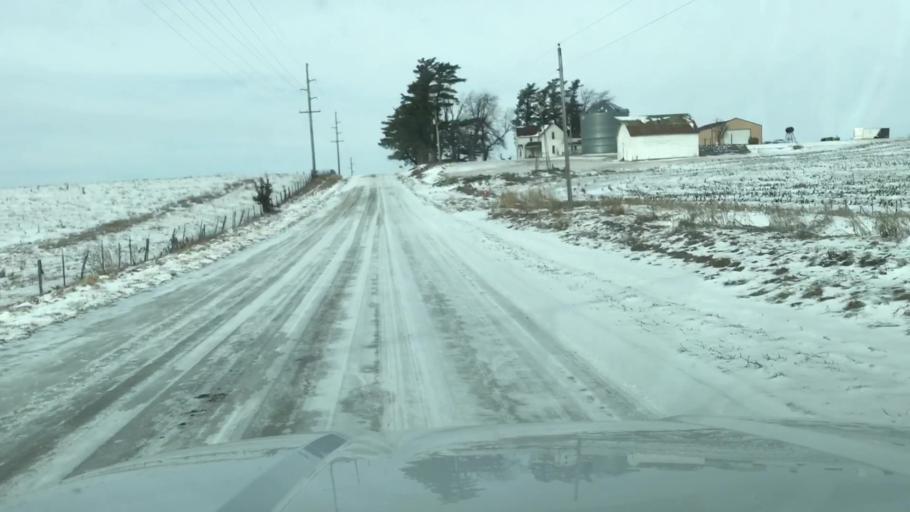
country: US
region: Missouri
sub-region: Holt County
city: Mound City
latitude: 40.1301
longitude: -95.0730
